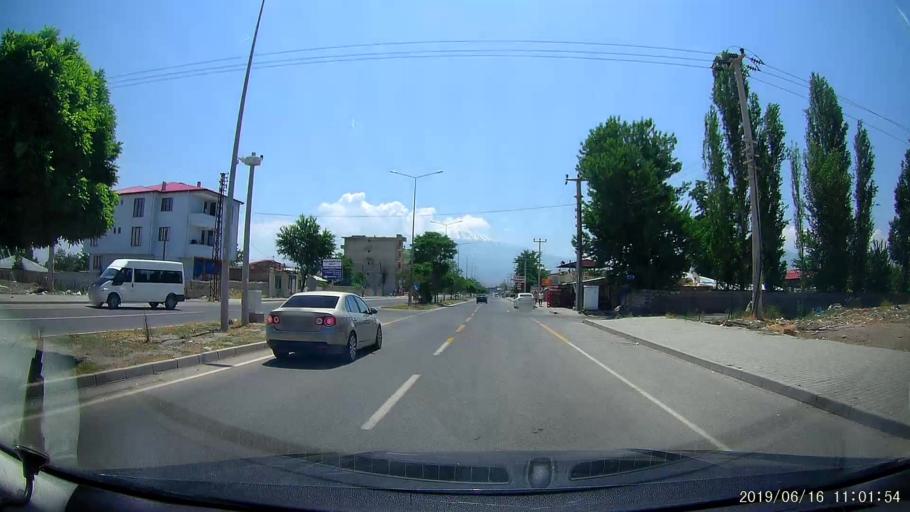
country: TR
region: Igdir
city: Igdir
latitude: 39.9115
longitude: 44.0547
